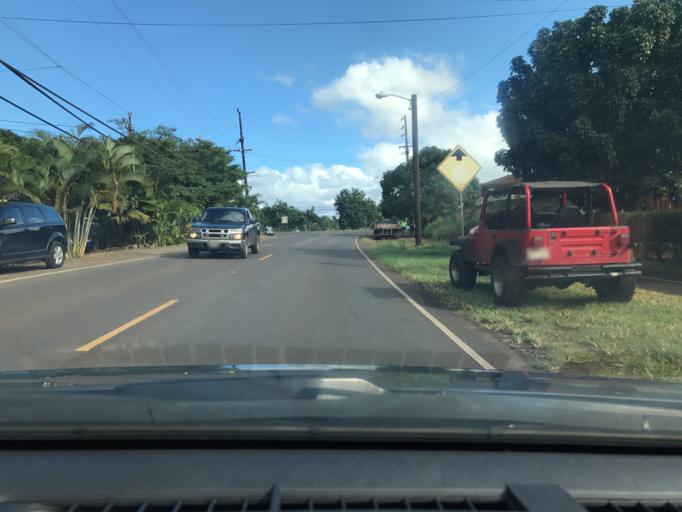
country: US
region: Hawaii
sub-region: Honolulu County
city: Hale'iwa
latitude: 21.5762
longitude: -158.1080
